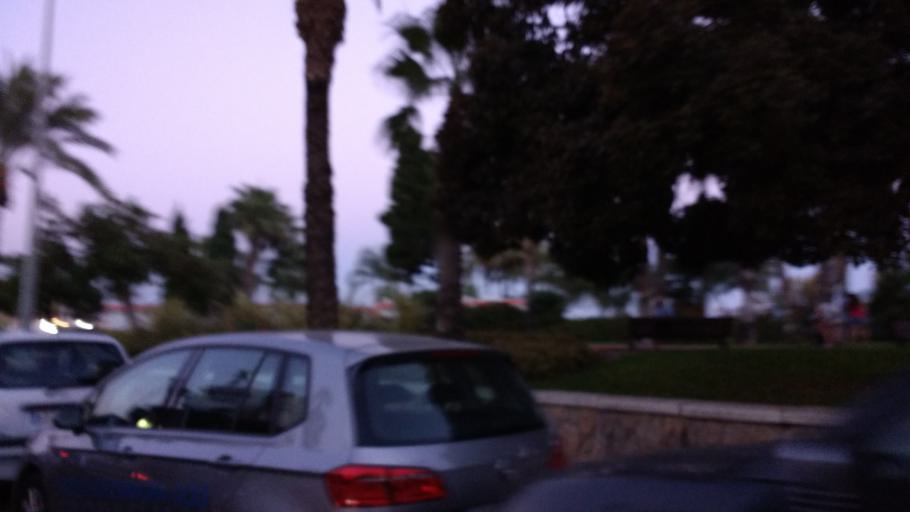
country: ES
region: Andalusia
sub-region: Provincia de Malaga
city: Velez-Malaga
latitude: 36.7395
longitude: -4.0924
